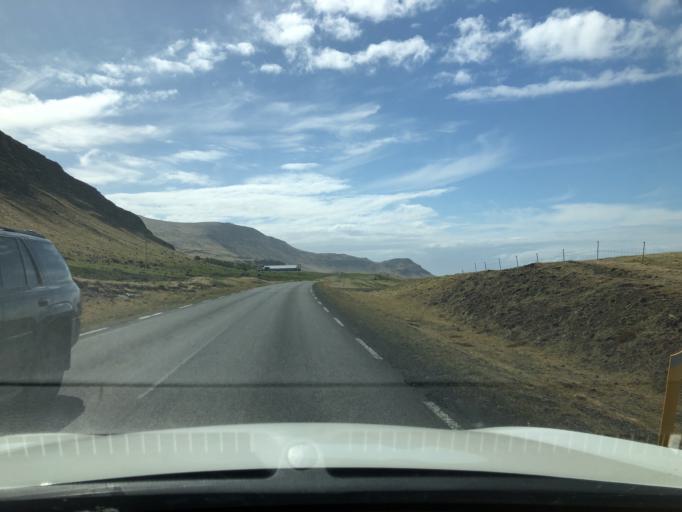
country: IS
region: Capital Region
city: Mosfellsbaer
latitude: 64.3122
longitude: -21.7702
